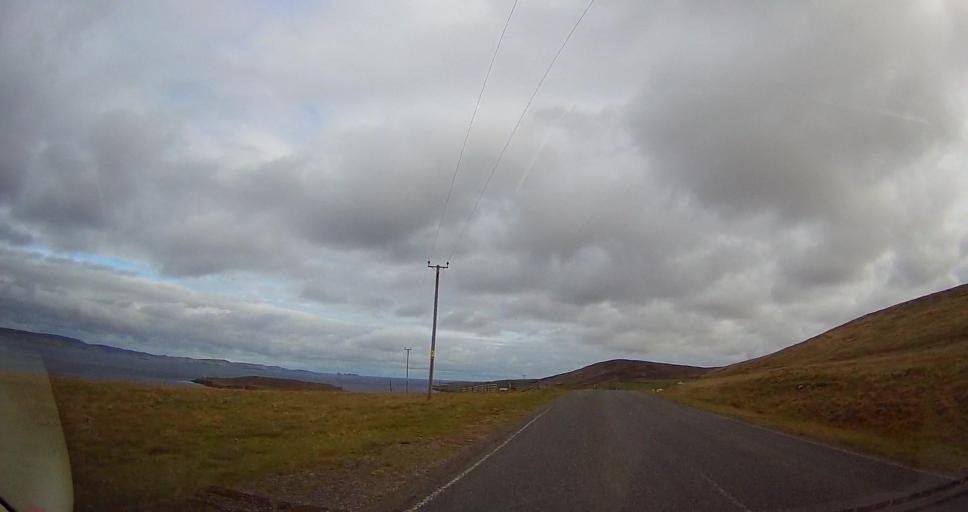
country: GB
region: Scotland
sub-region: Shetland Islands
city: Shetland
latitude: 60.5093
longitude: -1.1664
